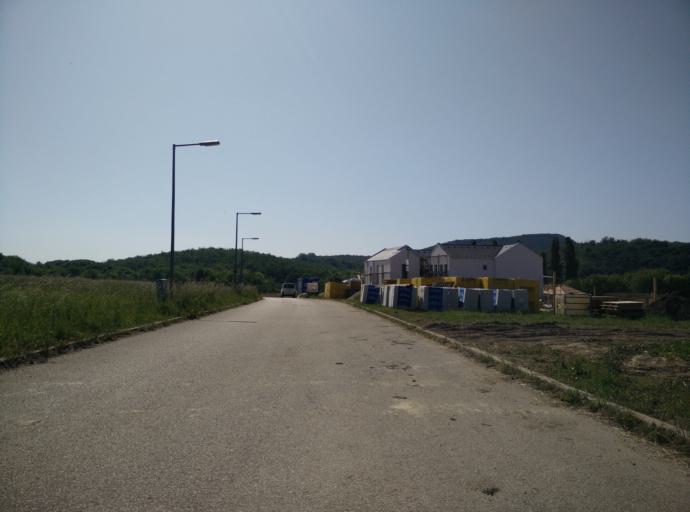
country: HU
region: Pest
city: Biatorbagy
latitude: 47.4723
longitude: 18.8422
